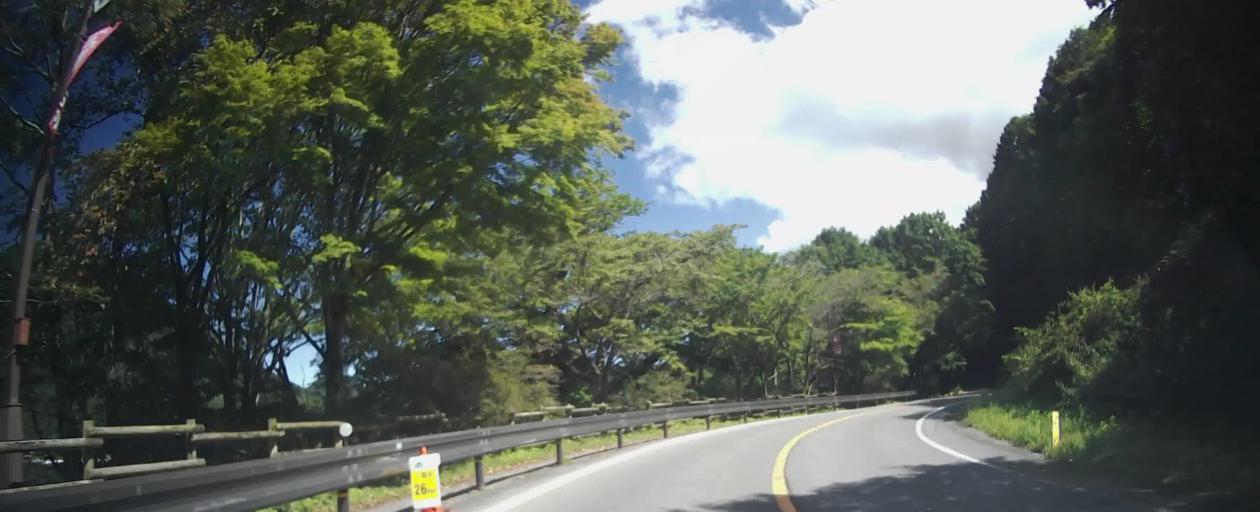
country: JP
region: Gunma
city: Nakanojomachi
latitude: 36.4683
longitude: 138.8701
